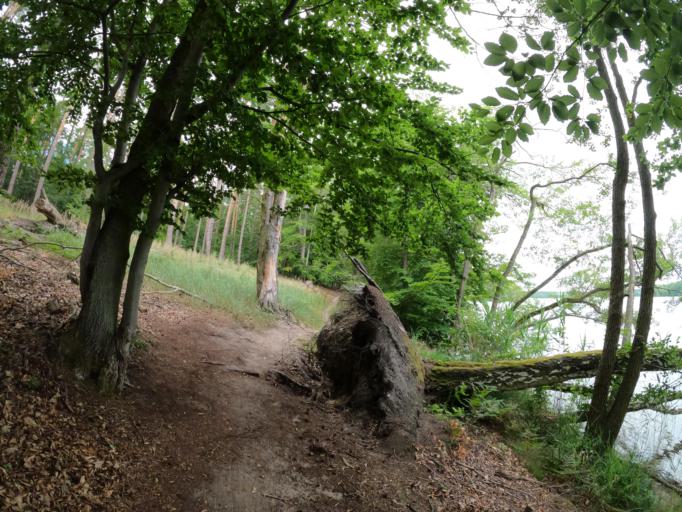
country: DE
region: Brandenburg
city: Angermunde
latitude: 53.0262
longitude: 13.9200
